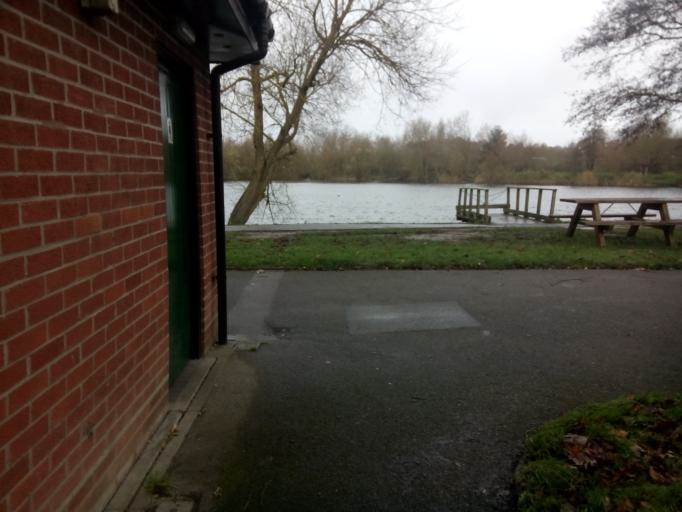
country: GB
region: England
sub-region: Suffolk
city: Needham Market
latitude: 52.1504
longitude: 1.0593
